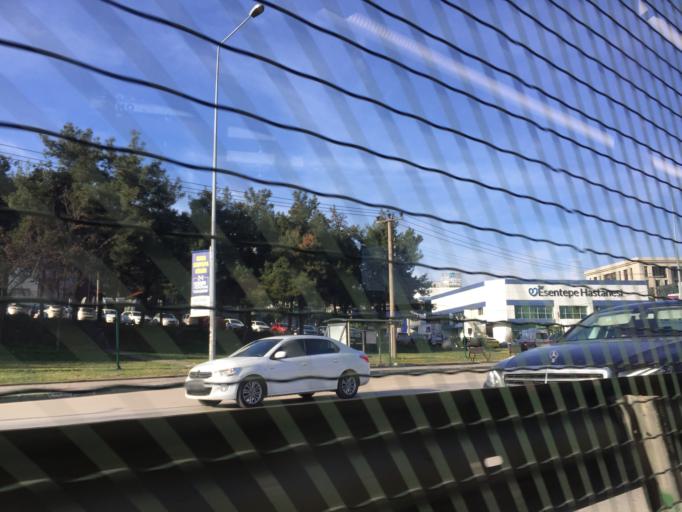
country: TR
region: Bursa
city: Yildirim
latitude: 40.2297
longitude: 28.9857
